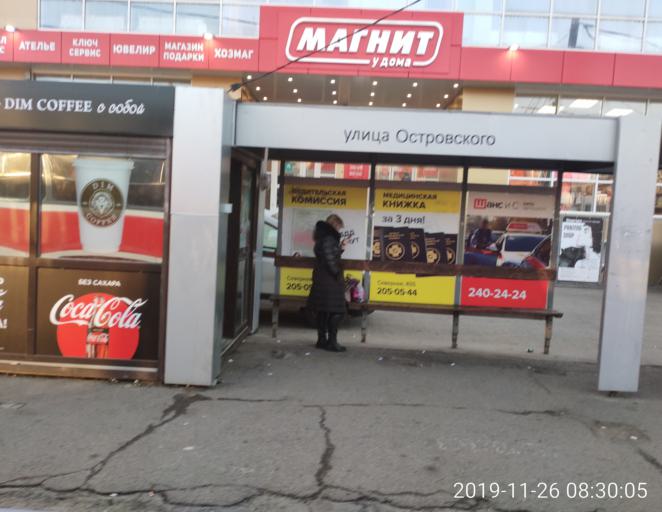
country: RU
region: Krasnodarskiy
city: Krasnodar
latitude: 45.0513
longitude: 39.0021
